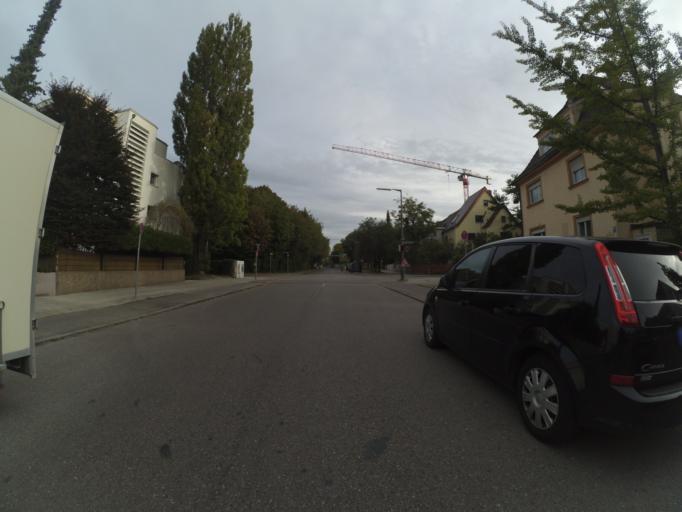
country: DE
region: Bavaria
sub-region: Upper Bavaria
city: Munich
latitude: 48.1643
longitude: 11.5198
